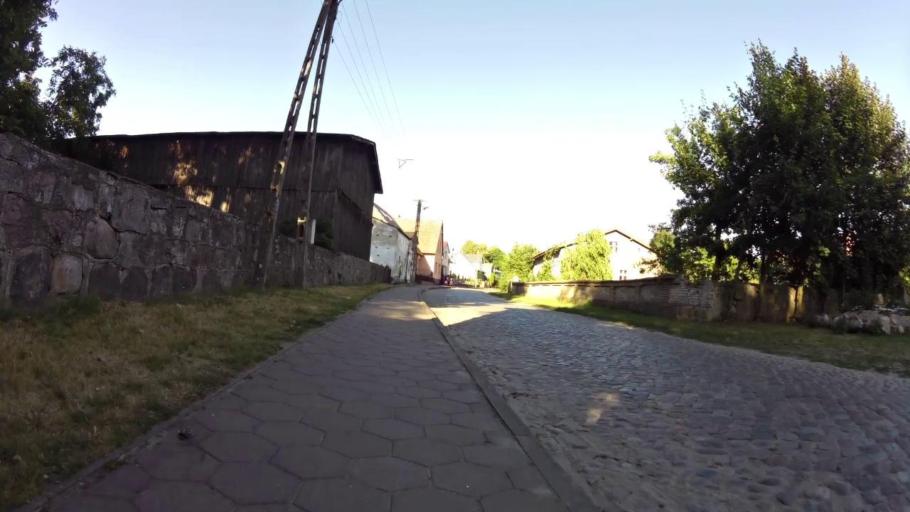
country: PL
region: West Pomeranian Voivodeship
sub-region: Powiat swidwinski
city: Swidwin
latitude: 53.7001
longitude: 15.8202
